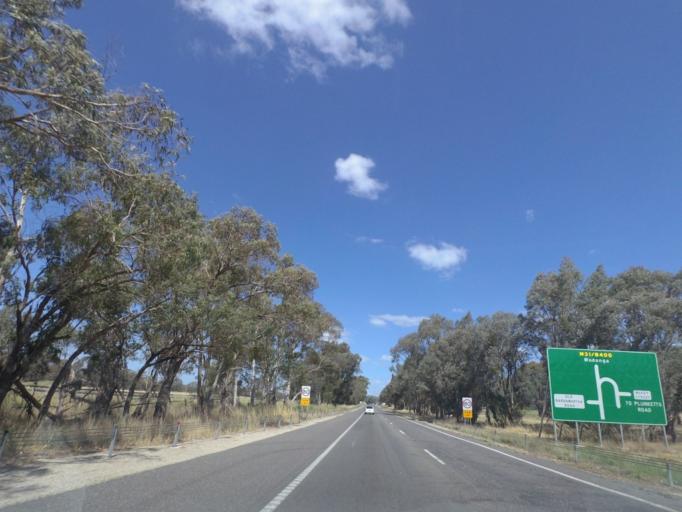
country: AU
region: Victoria
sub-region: Wodonga
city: Wodonga
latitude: -36.0991
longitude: 146.8201
